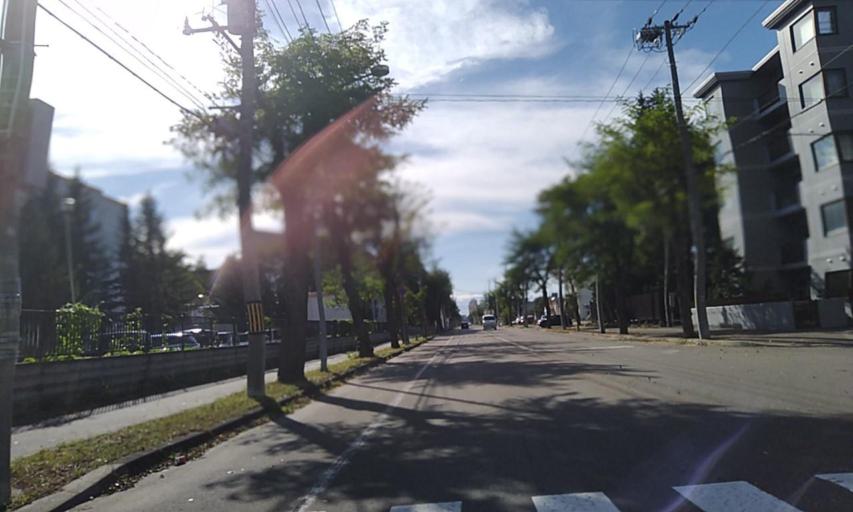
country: JP
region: Hokkaido
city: Obihiro
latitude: 42.9201
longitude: 143.2179
